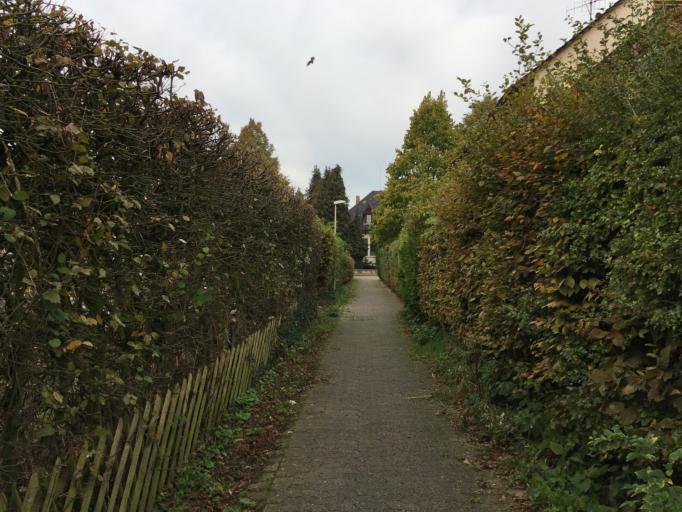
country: DE
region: Lower Saxony
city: Bad Munder am Deister
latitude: 52.1969
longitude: 9.4605
